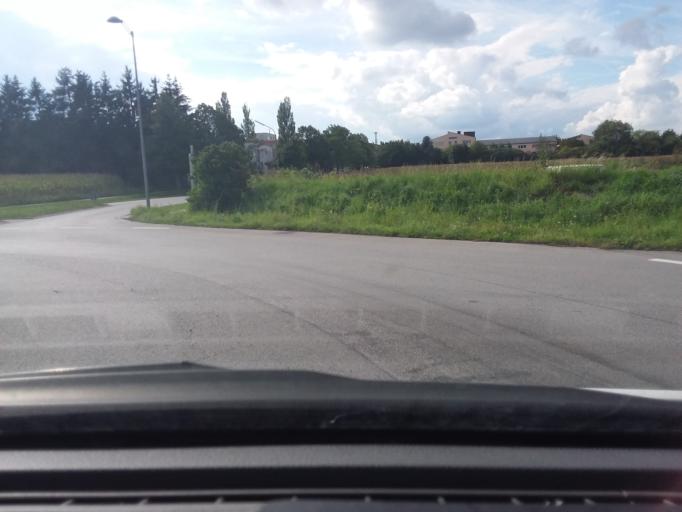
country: DE
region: Bavaria
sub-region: Upper Bavaria
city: Garching bei Munchen
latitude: 48.2525
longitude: 11.6315
